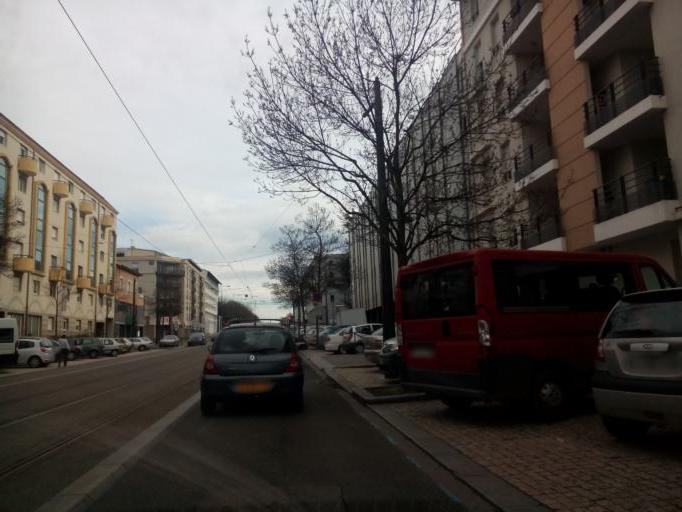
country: FR
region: Rhone-Alpes
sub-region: Departement du Rhone
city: Bron
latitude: 45.7313
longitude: 4.9155
